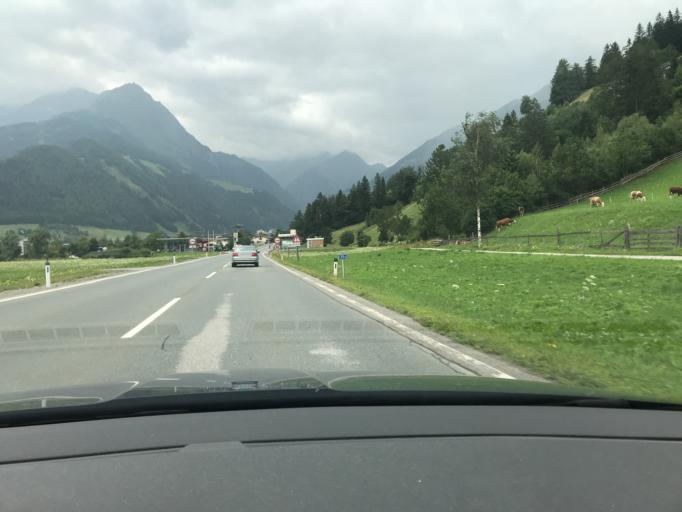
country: AT
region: Tyrol
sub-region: Politischer Bezirk Lienz
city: Matrei in Osttirol
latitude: 46.9881
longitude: 12.5462
